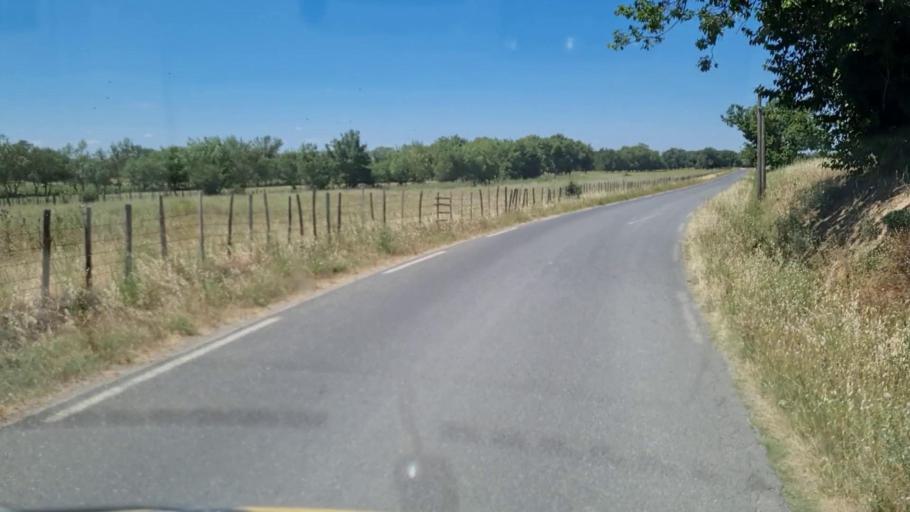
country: FR
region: Languedoc-Roussillon
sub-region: Departement du Gard
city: Le Cailar
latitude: 43.6443
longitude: 4.2523
